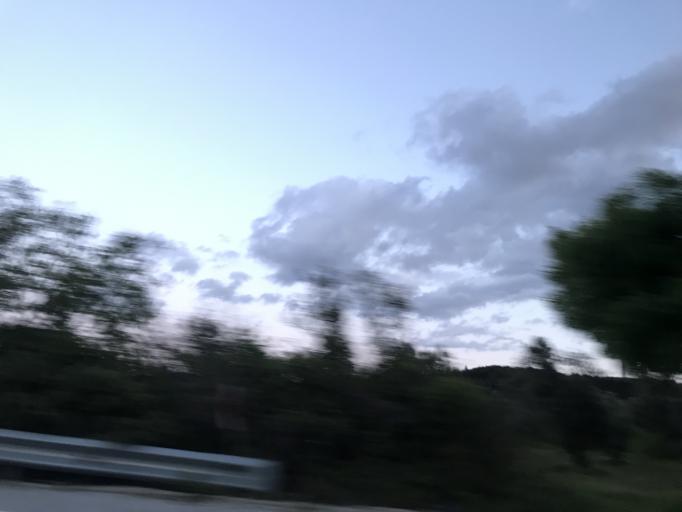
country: TR
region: Hatay
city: Buyukcat
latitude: 36.1089
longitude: 36.0454
